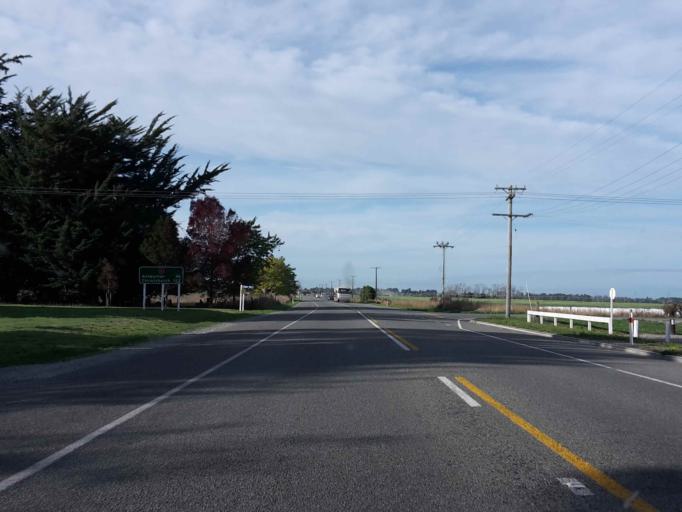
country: NZ
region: Canterbury
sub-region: Timaru District
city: Pleasant Point
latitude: -44.0657
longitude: 171.3731
